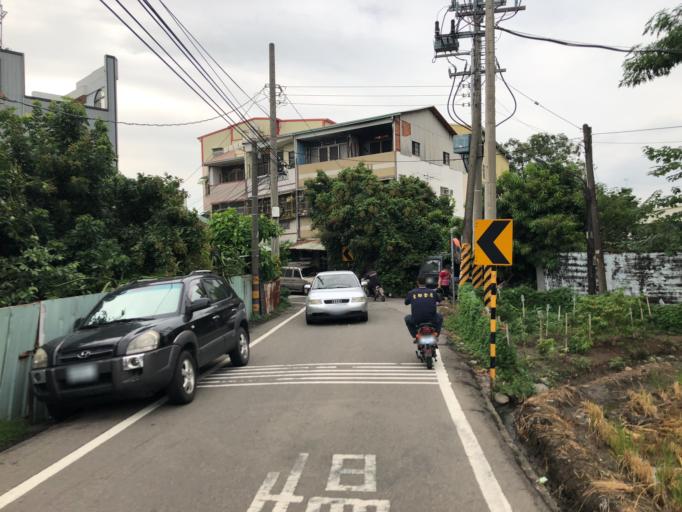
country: TW
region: Taiwan
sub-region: Taichung City
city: Taichung
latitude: 24.0613
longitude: 120.6822
